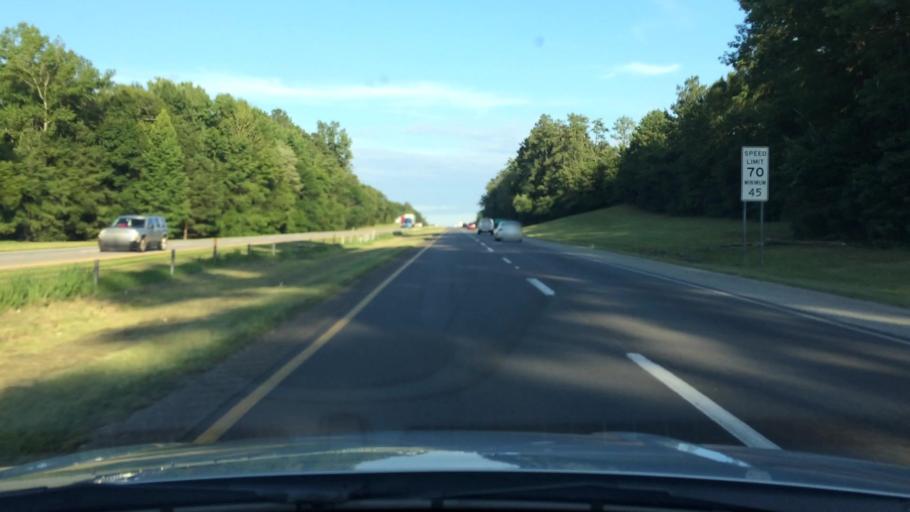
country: US
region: South Carolina
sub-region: Newberry County
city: Prosperity
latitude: 34.2874
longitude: -81.5369
